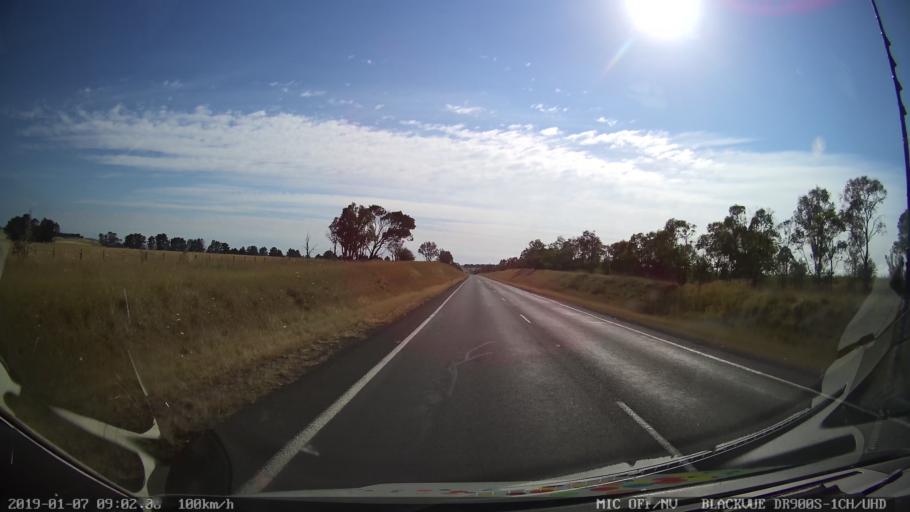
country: AU
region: New South Wales
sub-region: Armidale Dumaresq
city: Armidale
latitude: -30.7368
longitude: 151.4178
